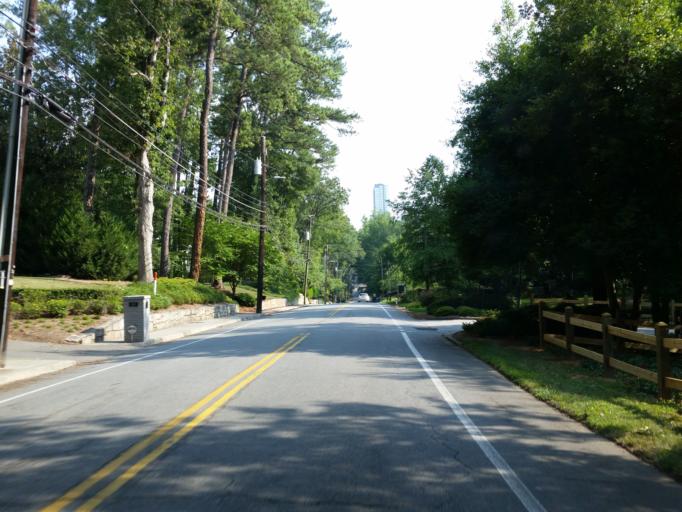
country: US
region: Georgia
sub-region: DeKalb County
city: North Atlanta
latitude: 33.8677
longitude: -84.3580
